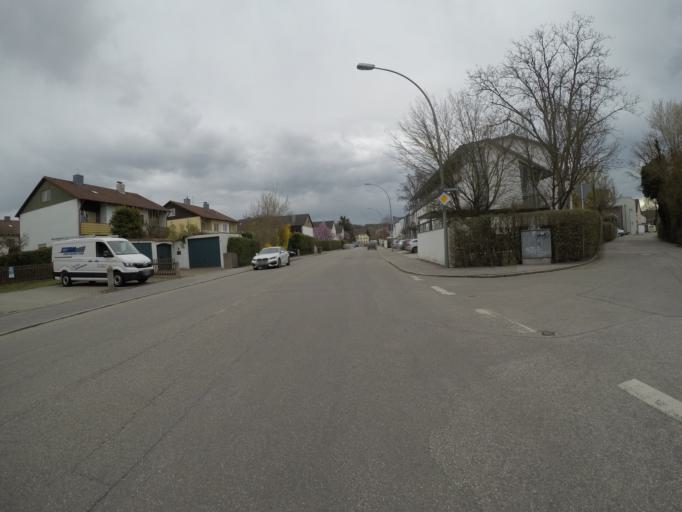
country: DE
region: Bavaria
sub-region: Lower Bavaria
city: Landshut
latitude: 48.5333
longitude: 12.1257
